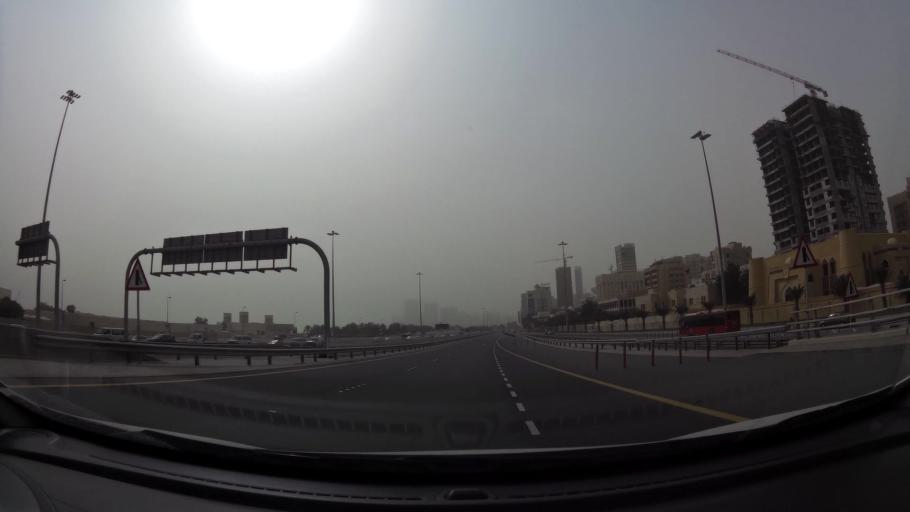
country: BH
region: Muharraq
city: Al Muharraq
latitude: 26.2405
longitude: 50.5950
